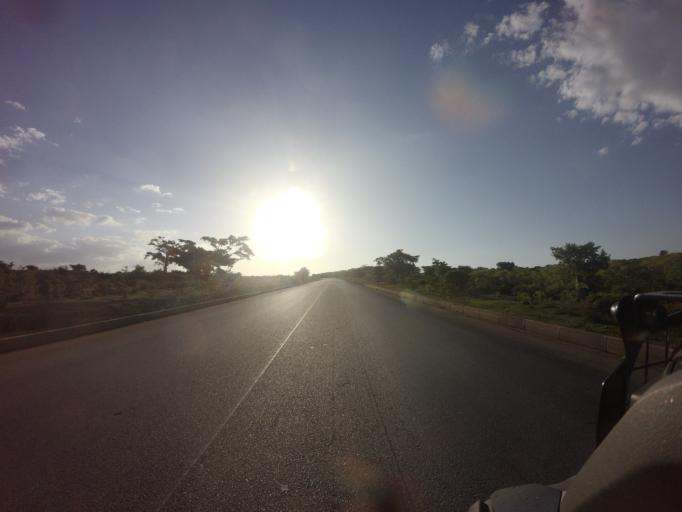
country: AO
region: Huila
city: Lubango
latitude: -14.7868
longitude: 13.7158
